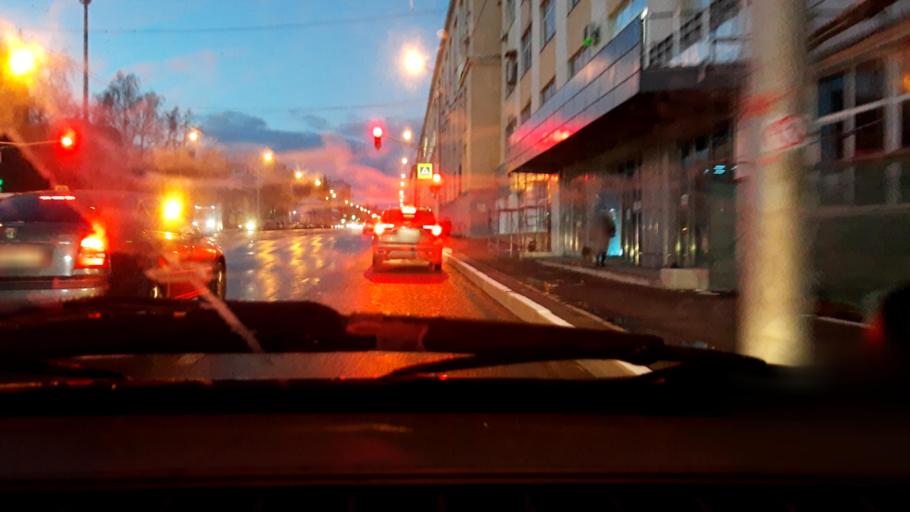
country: RU
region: Bashkortostan
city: Ufa
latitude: 54.7358
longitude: 55.9389
